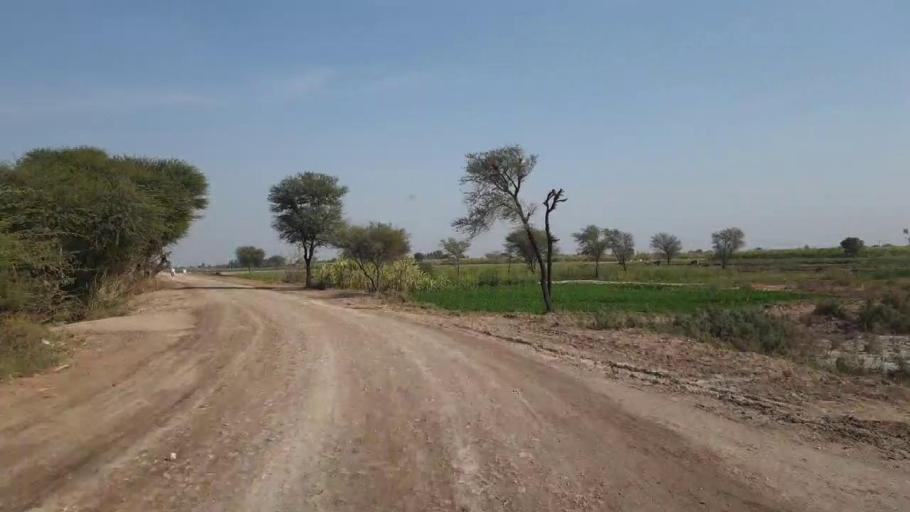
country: PK
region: Sindh
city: Chambar
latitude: 25.3343
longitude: 68.7714
